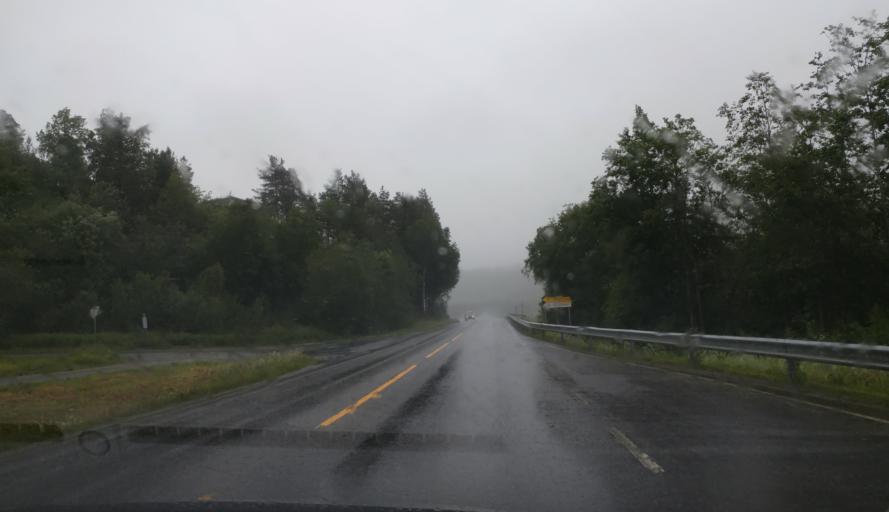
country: NO
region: Nord-Trondelag
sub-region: Stjordal
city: Stjordalshalsen
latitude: 63.3939
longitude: 10.9661
